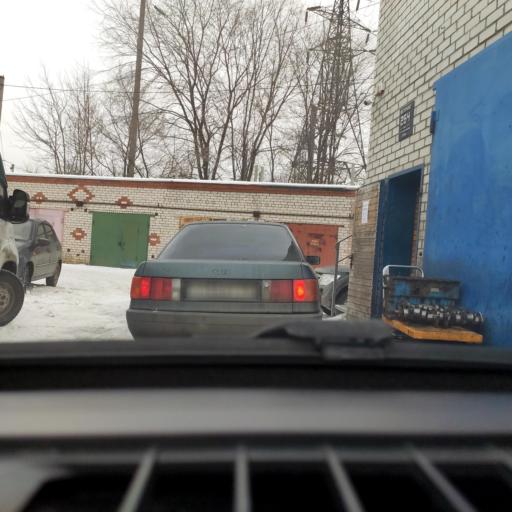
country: RU
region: Voronezj
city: Voronezh
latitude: 51.6885
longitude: 39.1458
